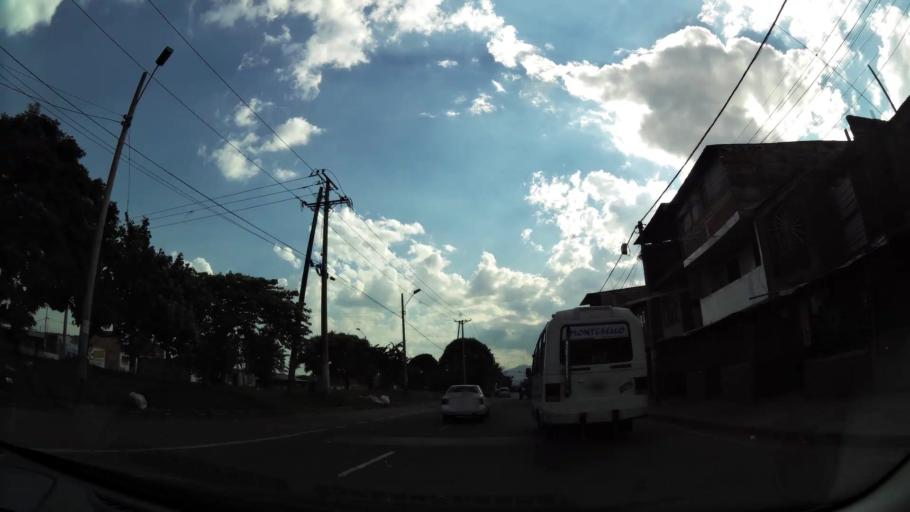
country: CO
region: Valle del Cauca
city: Cali
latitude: 3.4137
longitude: -76.4903
